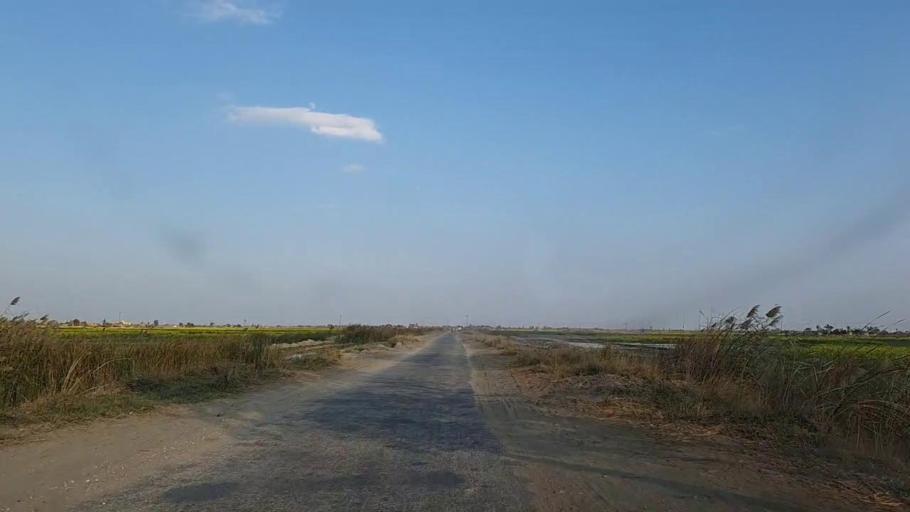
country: PK
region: Sindh
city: Sanghar
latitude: 26.2644
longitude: 68.9387
